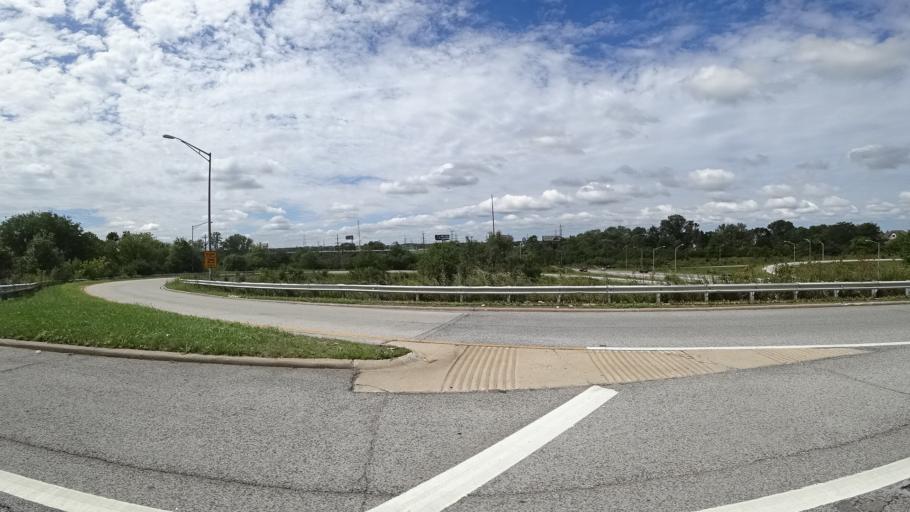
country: US
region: Illinois
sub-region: Cook County
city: Burbank
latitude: 41.7186
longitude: -87.7986
